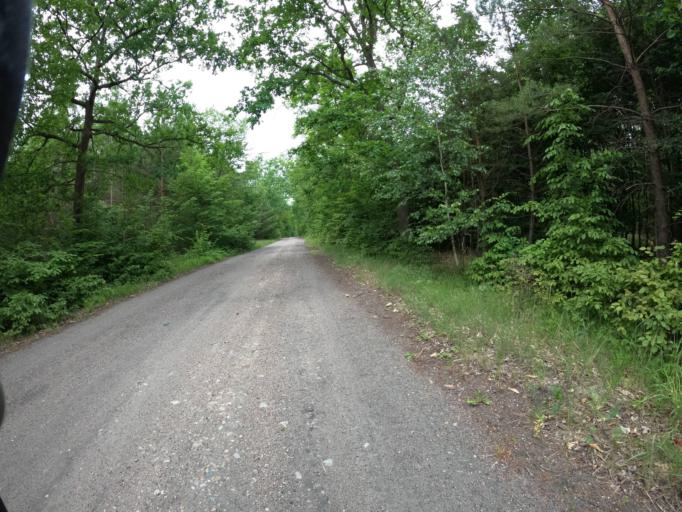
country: PL
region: West Pomeranian Voivodeship
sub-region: Powiat gryfinski
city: Mieszkowice
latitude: 52.7245
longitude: 14.4873
